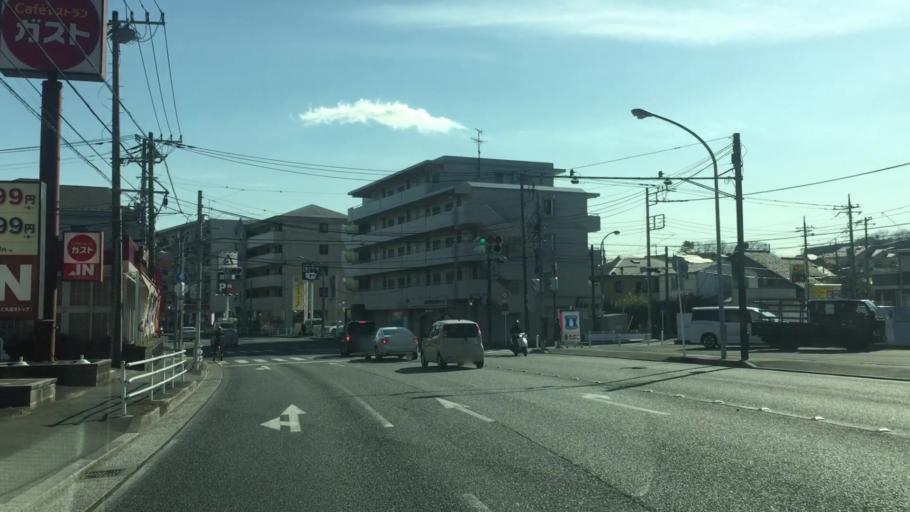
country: JP
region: Kanagawa
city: Zushi
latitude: 35.3476
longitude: 139.6083
